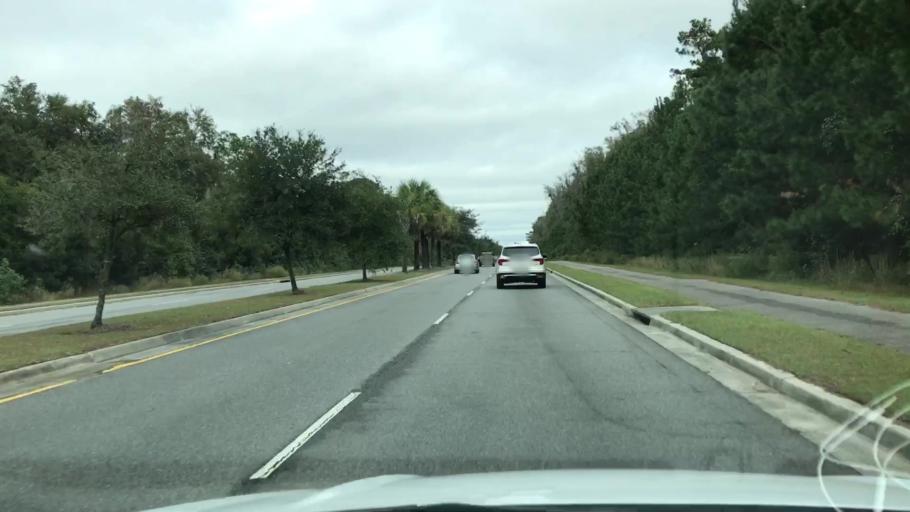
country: US
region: South Carolina
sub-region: Beaufort County
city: Bluffton
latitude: 32.2591
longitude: -80.8899
